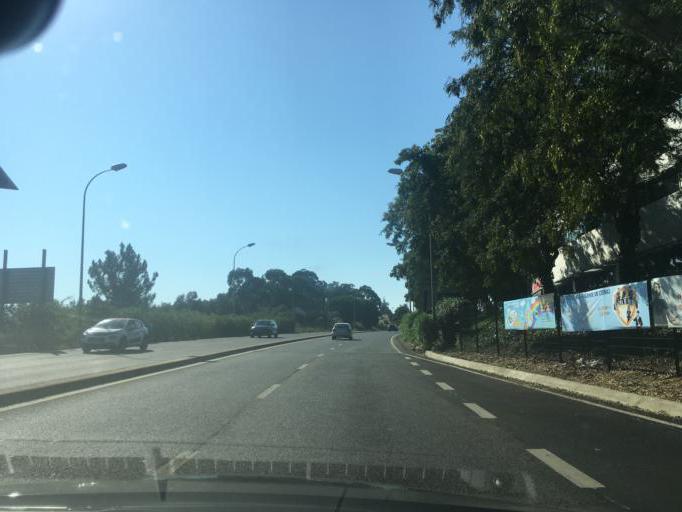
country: PT
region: Lisbon
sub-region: Oeiras
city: Porto Salvo
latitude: 38.7113
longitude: -9.2983
